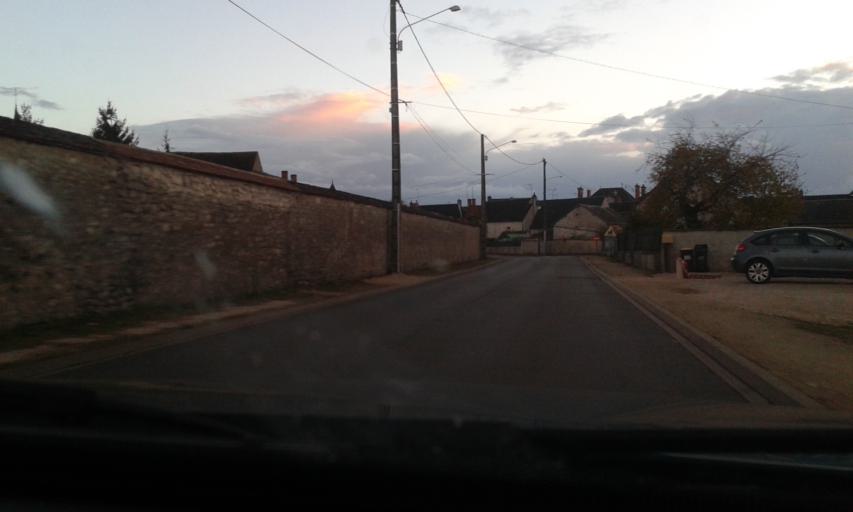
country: FR
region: Centre
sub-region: Departement du Loiret
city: Huisseau-sur-Mauves
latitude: 47.8940
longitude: 1.7041
